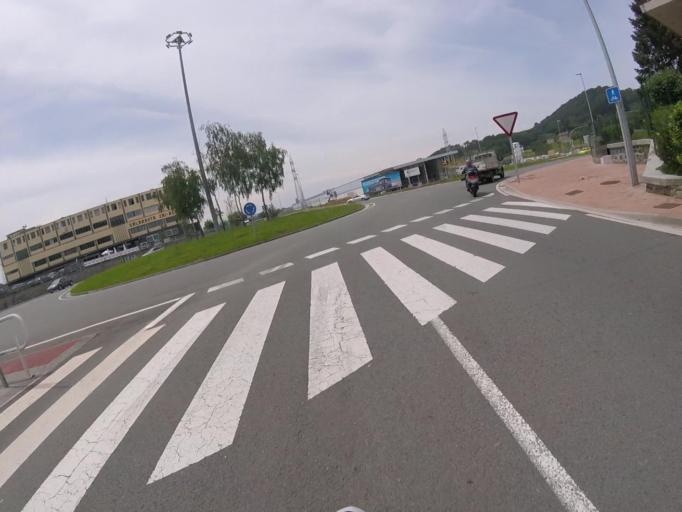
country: ES
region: Basque Country
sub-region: Provincia de Guipuzcoa
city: Hernani
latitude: 43.2771
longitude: -1.9870
